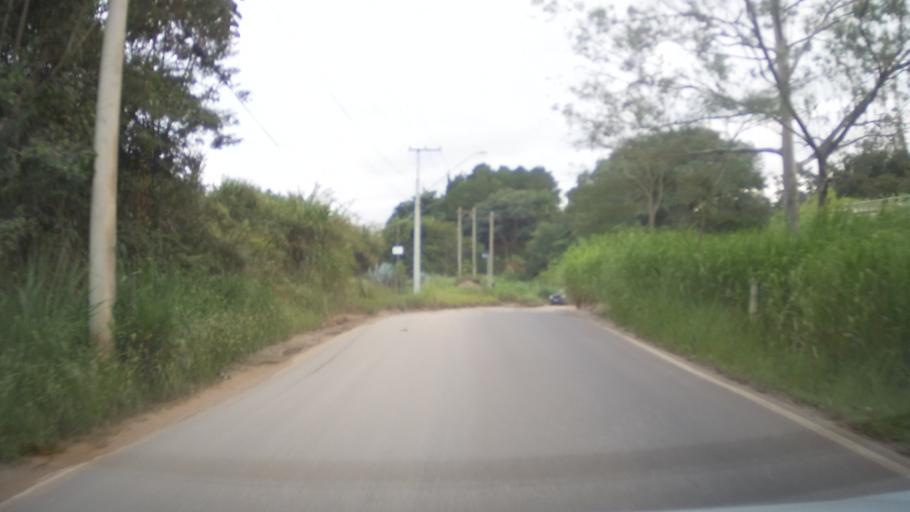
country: BR
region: Sao Paulo
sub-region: Vinhedo
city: Vinhedo
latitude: -23.0674
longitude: -47.0325
